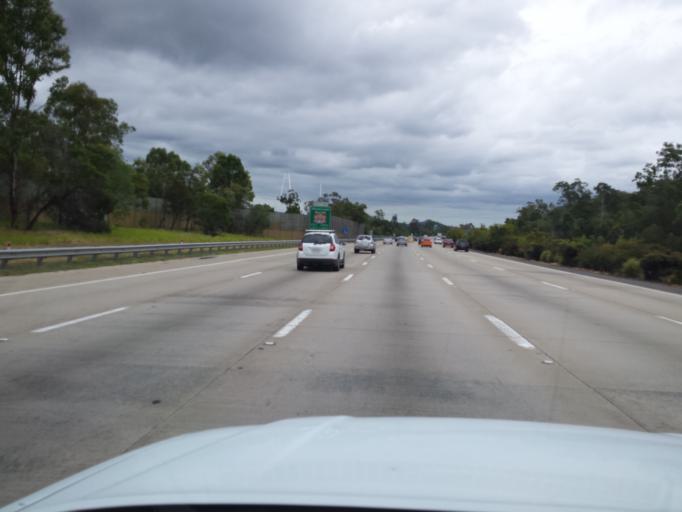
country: AU
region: Queensland
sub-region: Gold Coast
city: Upper Coomera
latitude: -27.9177
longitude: 153.3214
